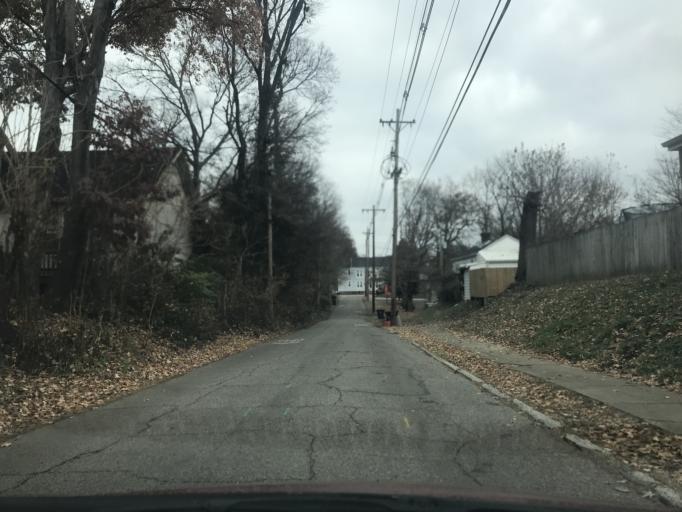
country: US
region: Kentucky
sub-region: Jefferson County
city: Louisville
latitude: 38.2374
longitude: -85.7310
